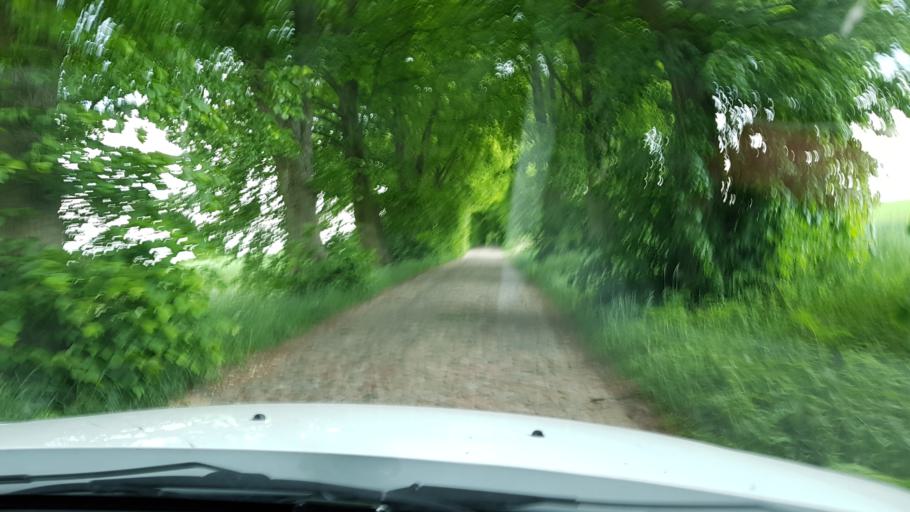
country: PL
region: West Pomeranian Voivodeship
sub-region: Powiat stargardzki
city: Stara Dabrowa
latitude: 53.3783
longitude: 15.1680
